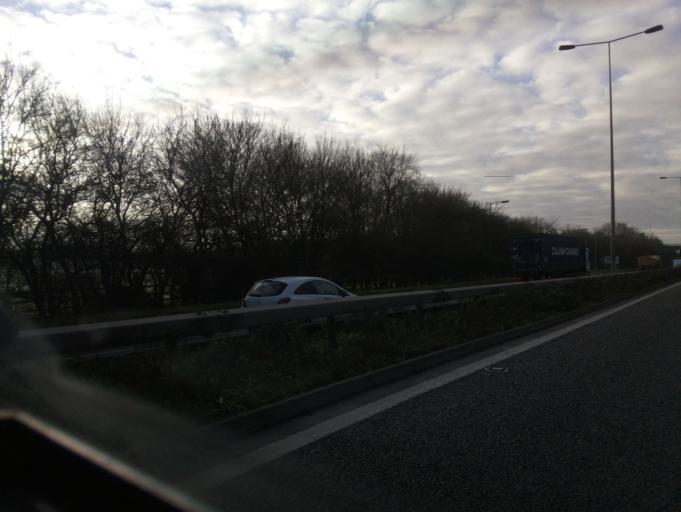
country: GB
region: England
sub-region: Staffordshire
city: Barton under Needwood
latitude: 52.7489
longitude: -1.7184
